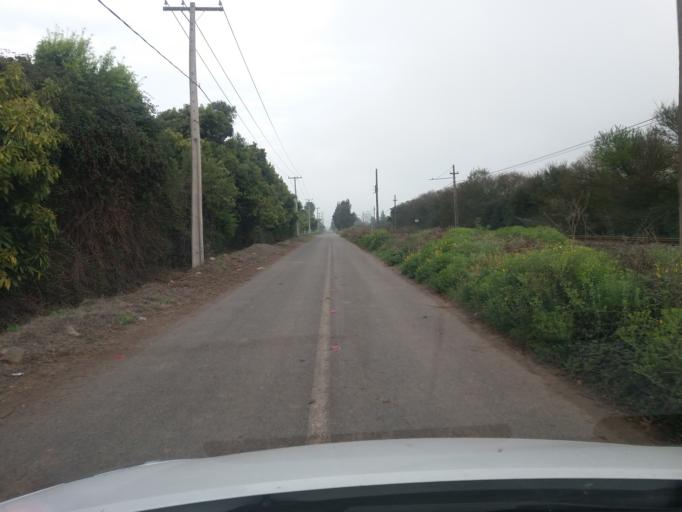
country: CL
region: Valparaiso
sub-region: Provincia de San Felipe
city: Llaillay
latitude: -32.8395
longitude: -71.0587
